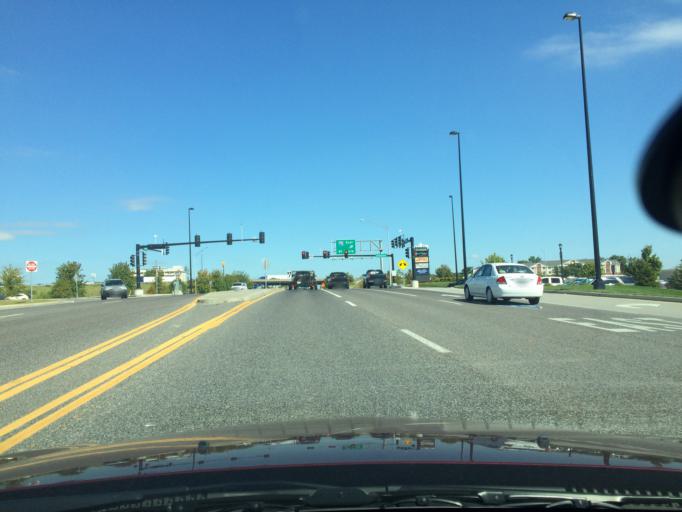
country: US
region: Missouri
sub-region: Saint Charles County
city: Saint Charles
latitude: 38.7663
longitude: -90.4959
